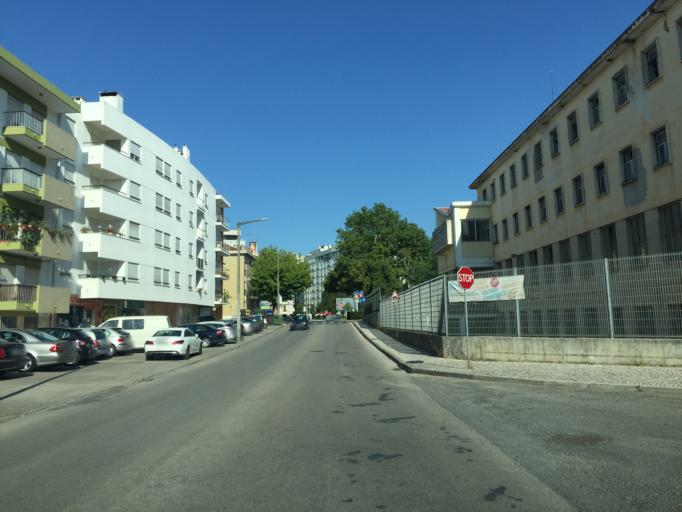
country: PT
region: Santarem
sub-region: Tomar
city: Tomar
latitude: 39.6046
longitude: -8.4047
